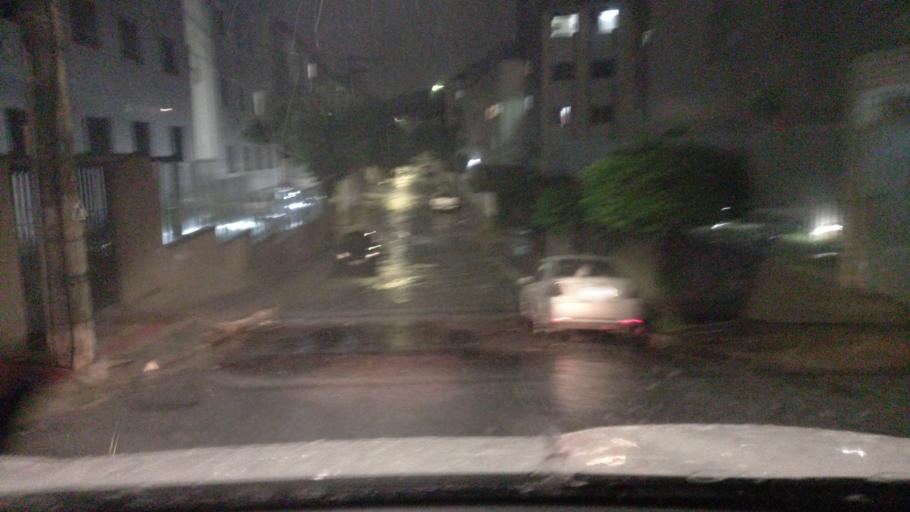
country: BR
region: Minas Gerais
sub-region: Belo Horizonte
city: Belo Horizonte
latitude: -19.9010
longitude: -43.9781
